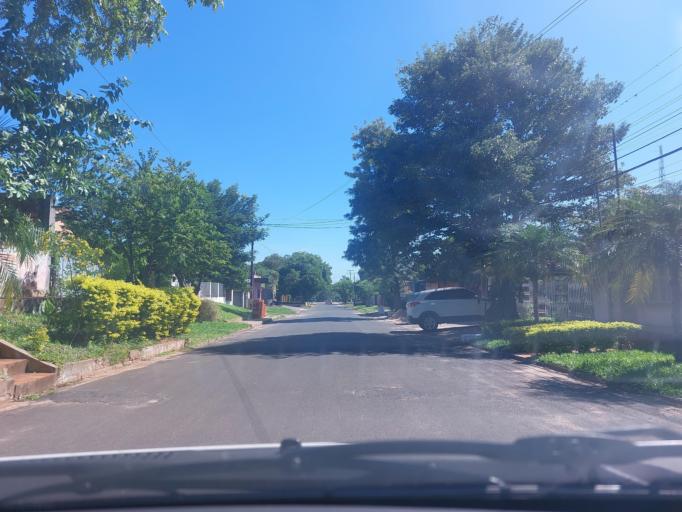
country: PY
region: San Pedro
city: Guayaybi
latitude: -24.6679
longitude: -56.4431
